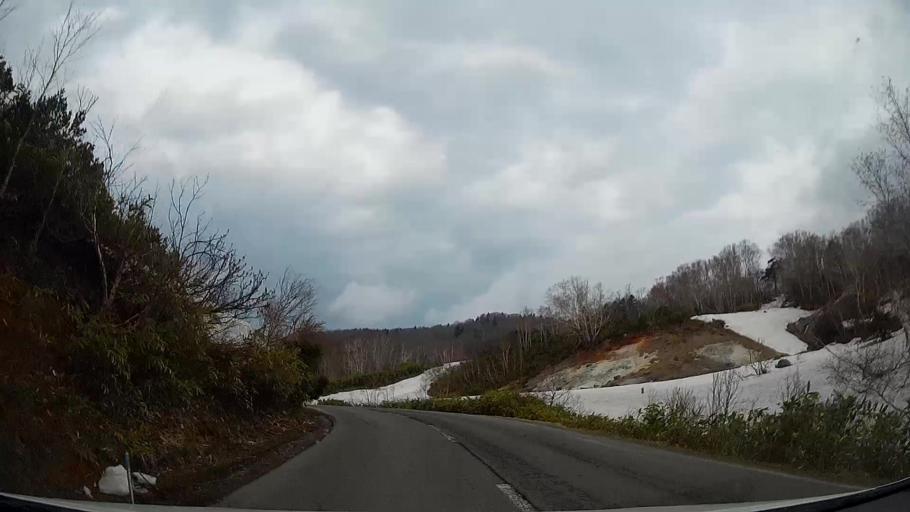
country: JP
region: Aomori
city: Aomori Shi
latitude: 40.6481
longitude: 140.8530
